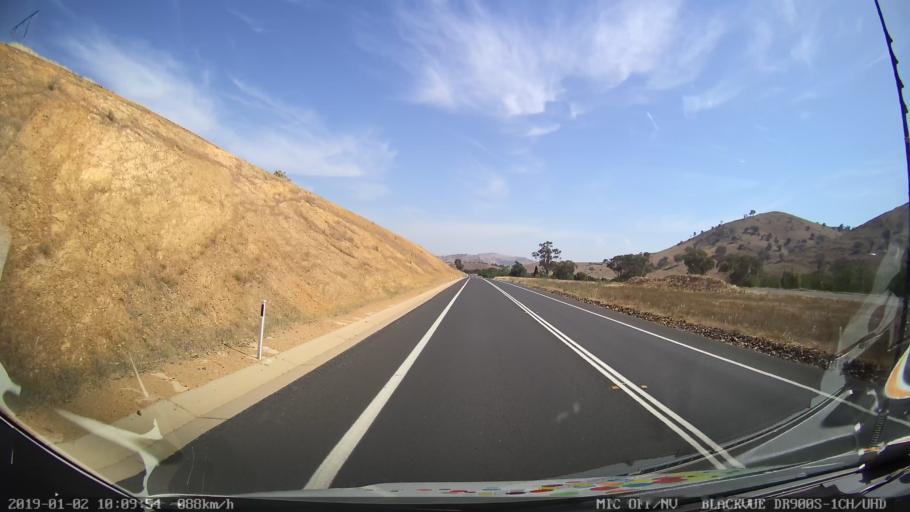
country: AU
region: New South Wales
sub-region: Gundagai
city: Gundagai
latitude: -35.1113
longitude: 148.0974
